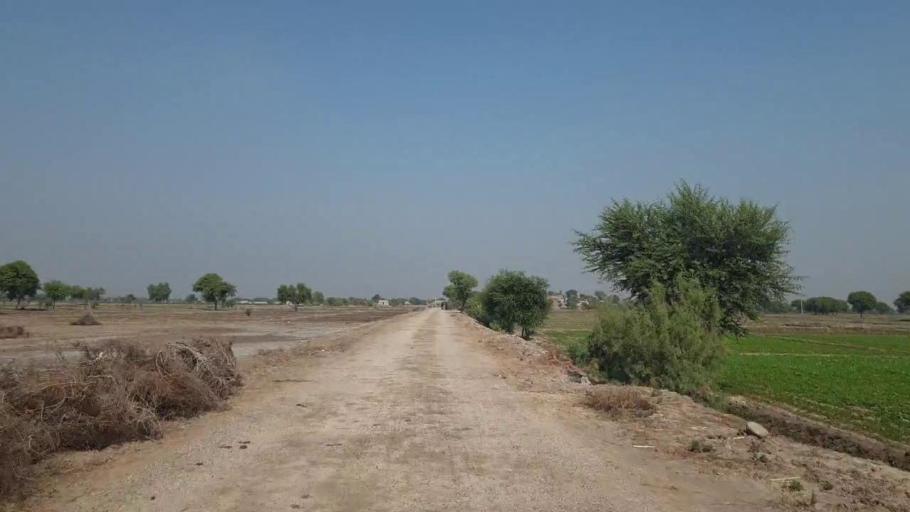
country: PK
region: Sindh
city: Sehwan
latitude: 26.4257
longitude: 67.7814
